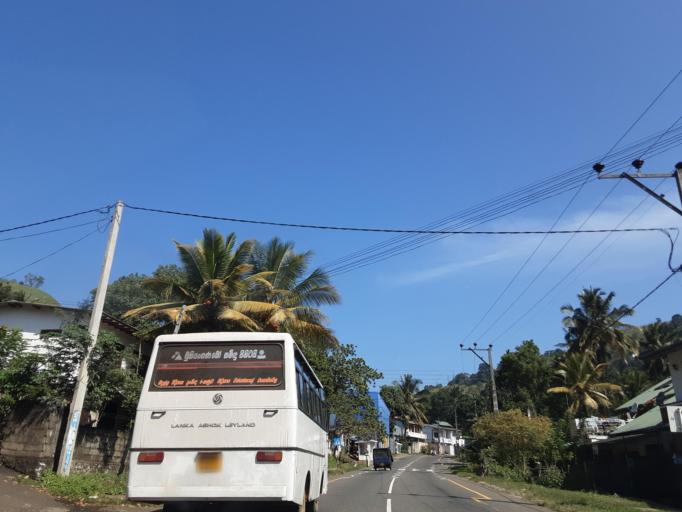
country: LK
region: Uva
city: Badulla
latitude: 7.0057
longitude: 81.0564
